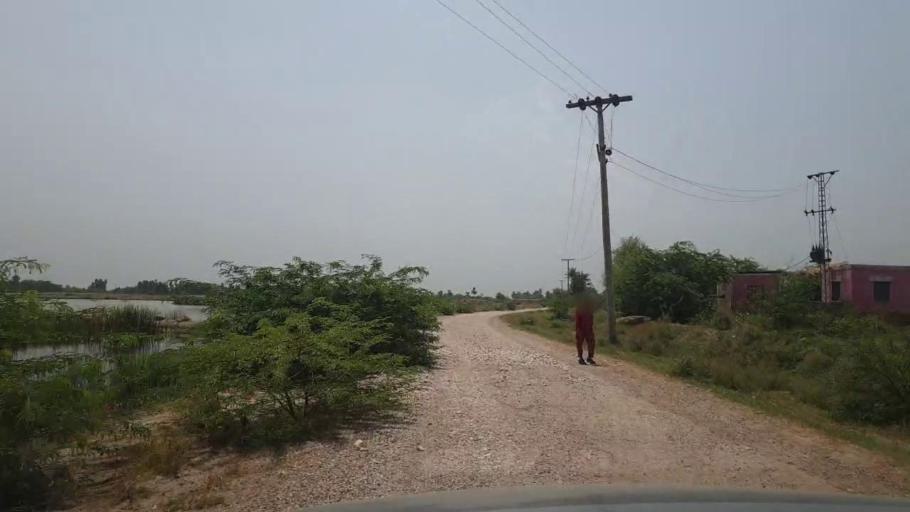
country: PK
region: Sindh
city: Garhi Yasin
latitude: 27.8840
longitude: 68.4955
